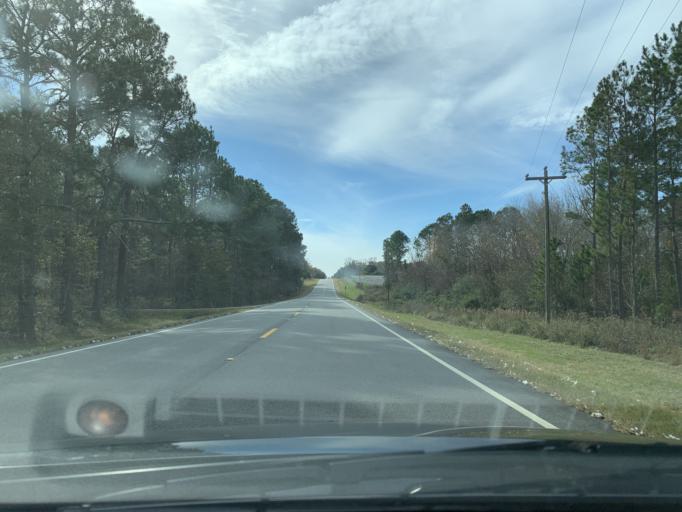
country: US
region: Georgia
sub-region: Turner County
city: Ashburn
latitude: 31.7682
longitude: -83.5337
